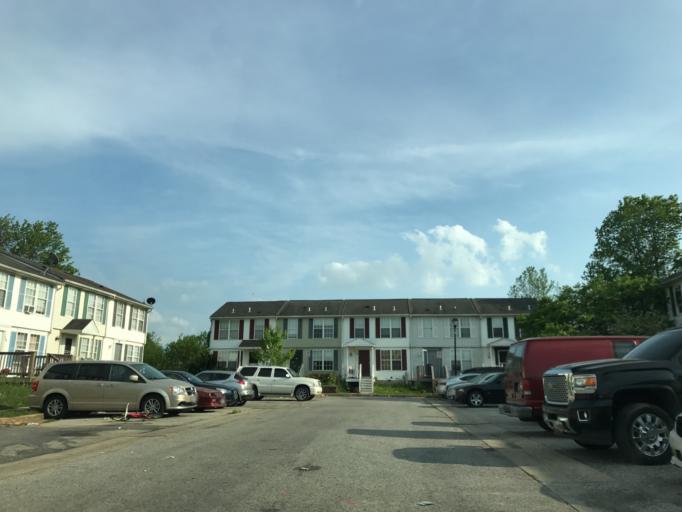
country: US
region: Maryland
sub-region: Baltimore County
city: Middle River
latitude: 39.3351
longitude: -76.4428
